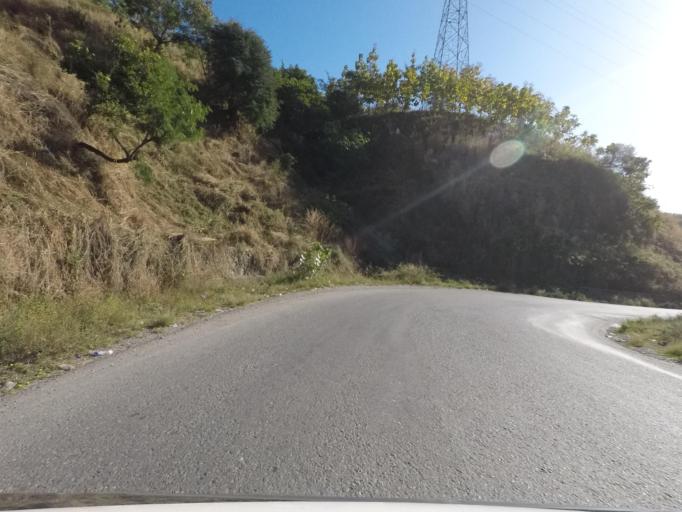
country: TL
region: Dili
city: Dili
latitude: -8.5630
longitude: 125.6336
